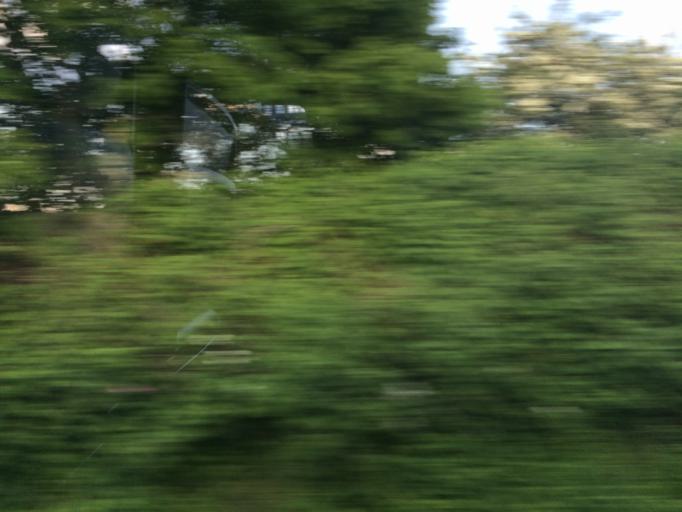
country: DE
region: North Rhine-Westphalia
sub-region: Regierungsbezirk Dusseldorf
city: Dusseldorf
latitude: 51.2833
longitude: 6.7881
